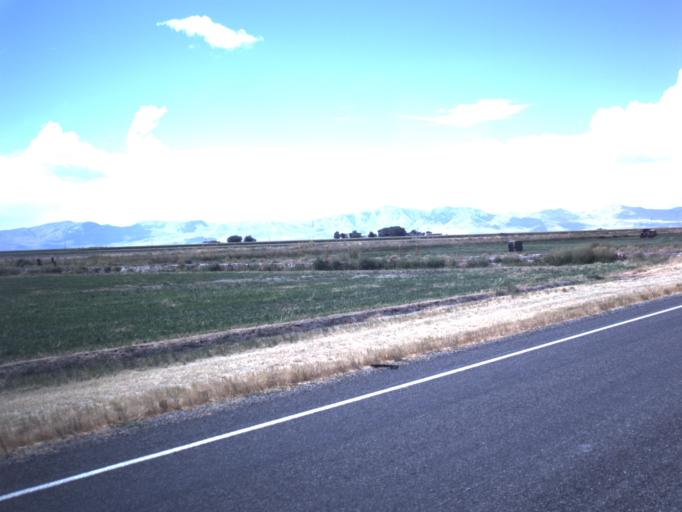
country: US
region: Utah
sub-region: Box Elder County
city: Elwood
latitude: 41.5700
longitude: -112.2014
